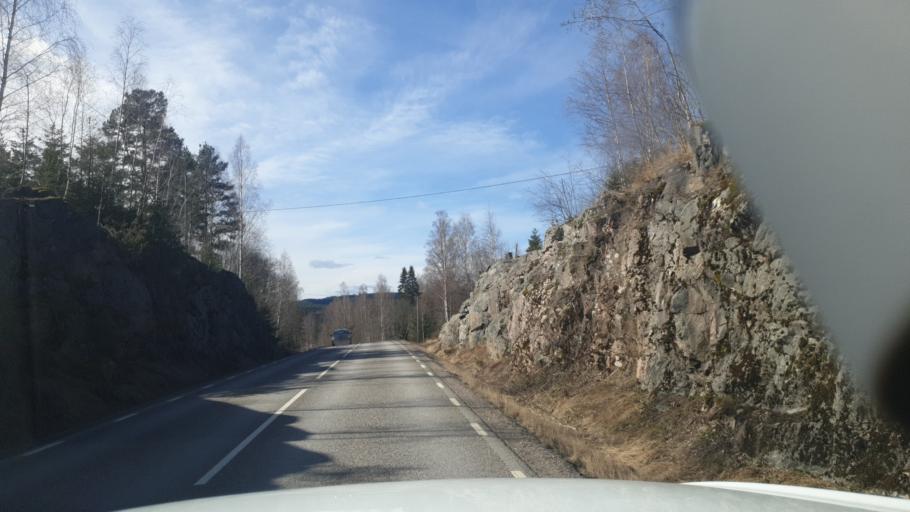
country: SE
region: Vaermland
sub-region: Eda Kommun
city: Amotfors
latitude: 59.6880
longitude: 12.4192
